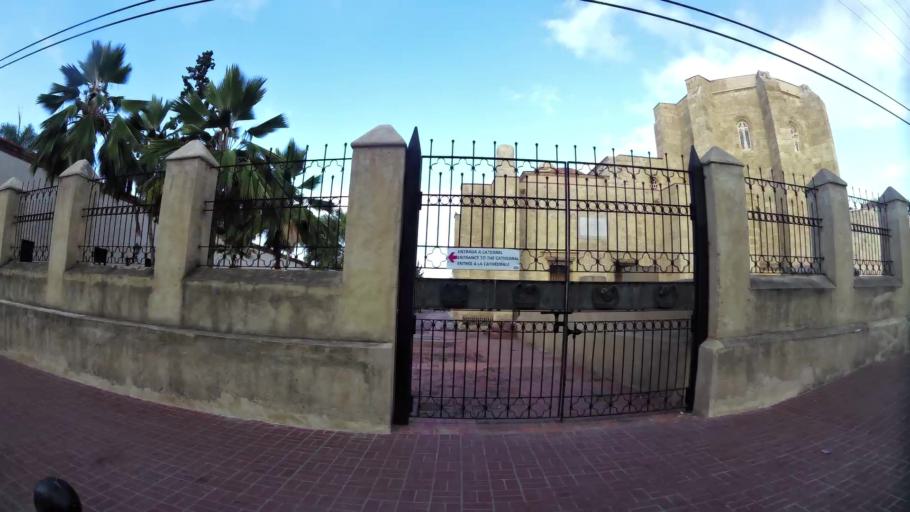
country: DO
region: Nacional
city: Ciudad Nueva
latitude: 18.4729
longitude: -69.8834
